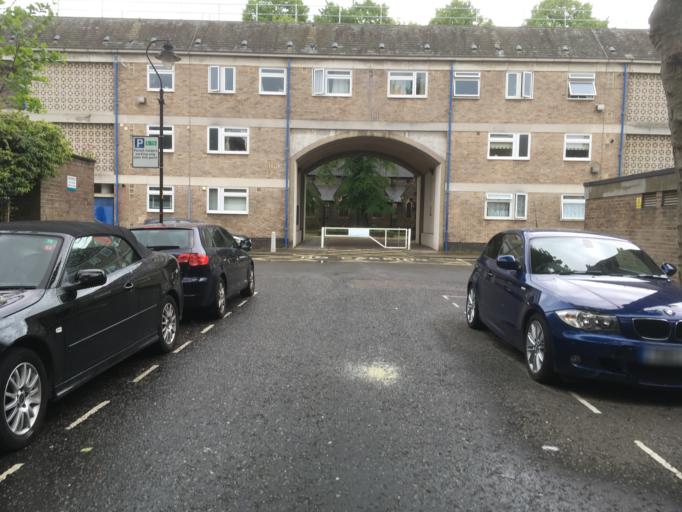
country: GB
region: England
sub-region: Greater London
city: Camberwell
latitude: 51.4918
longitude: -0.0688
